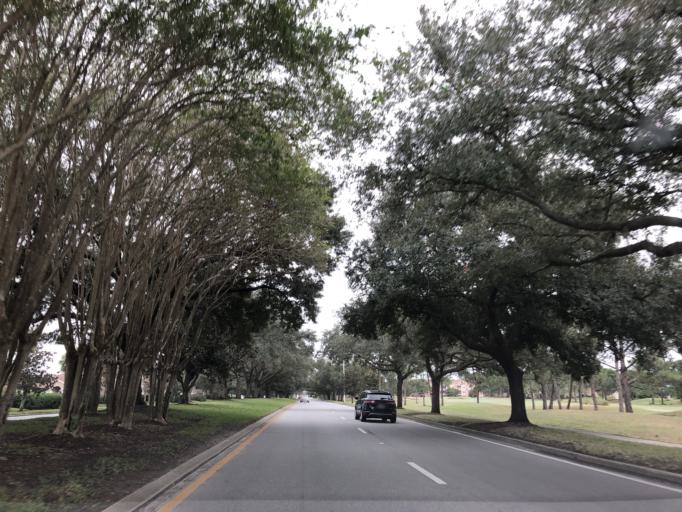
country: US
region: Florida
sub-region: Orange County
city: Hunters Creek
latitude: 28.3677
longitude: -81.4113
